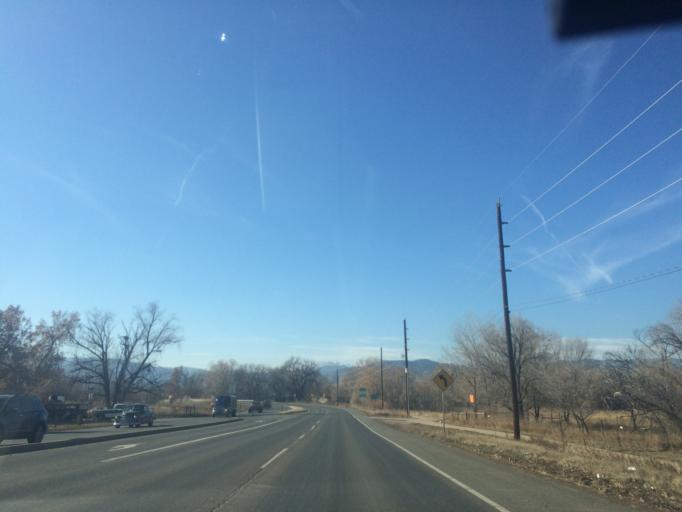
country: US
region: Colorado
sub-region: Boulder County
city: Boulder
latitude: 40.0293
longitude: -105.2199
